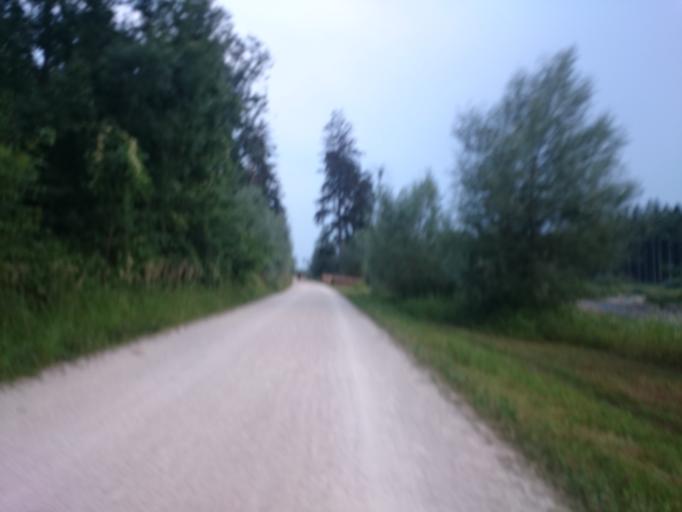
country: DE
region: Bavaria
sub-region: Swabia
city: Stadtbergen
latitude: 48.3274
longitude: 10.8500
